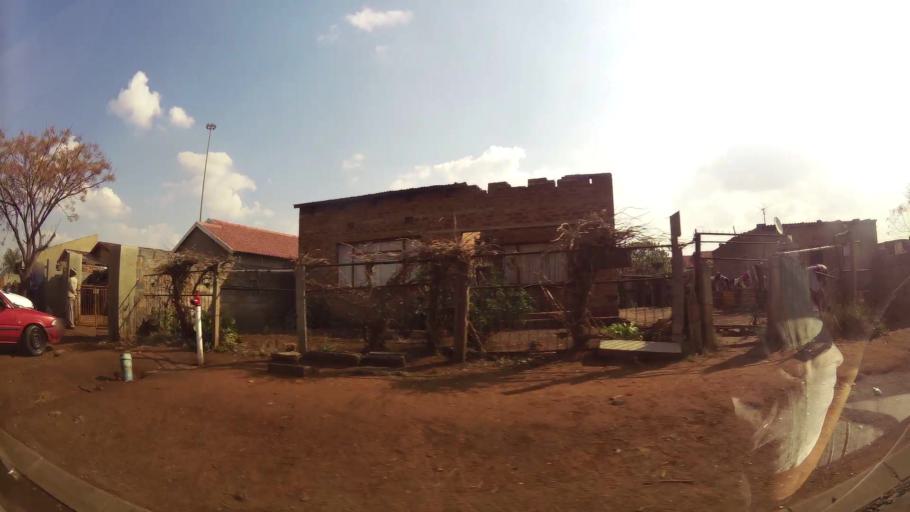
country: ZA
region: Gauteng
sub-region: Ekurhuleni Metropolitan Municipality
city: Germiston
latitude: -26.3036
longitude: 28.1520
